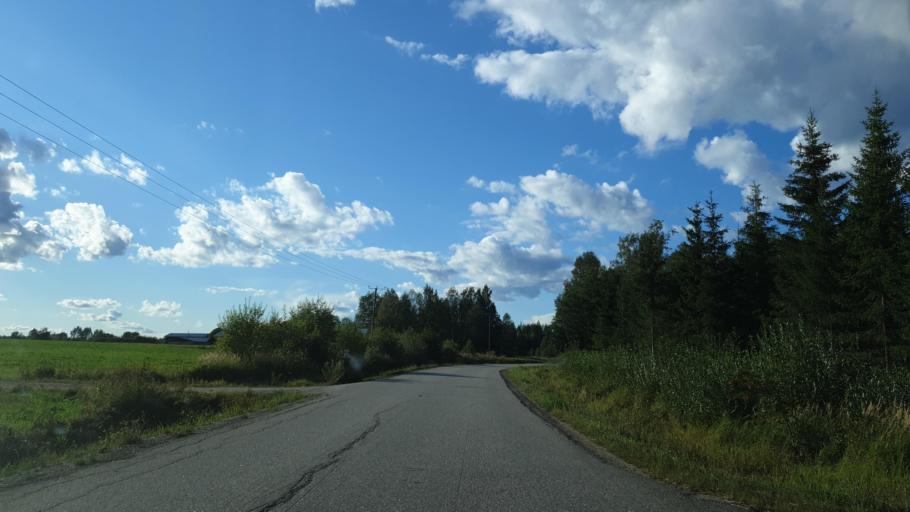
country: FI
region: Northern Savo
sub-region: Koillis-Savo
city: Kaavi
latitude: 62.9936
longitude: 28.7212
